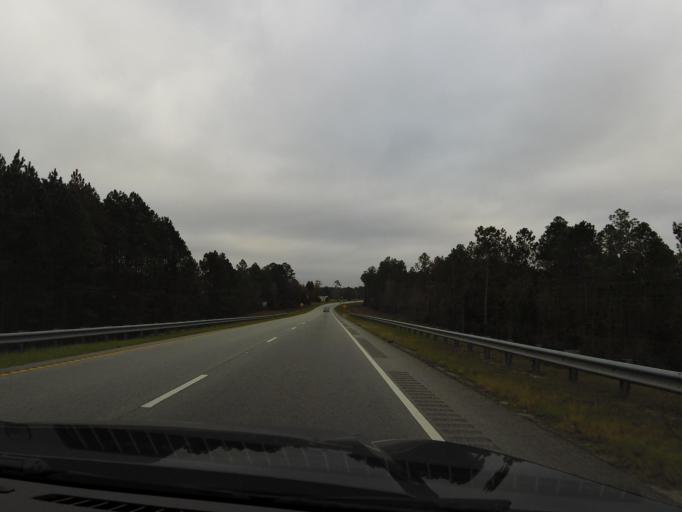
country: US
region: Georgia
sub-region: Charlton County
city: Folkston
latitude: 30.8666
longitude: -82.0163
